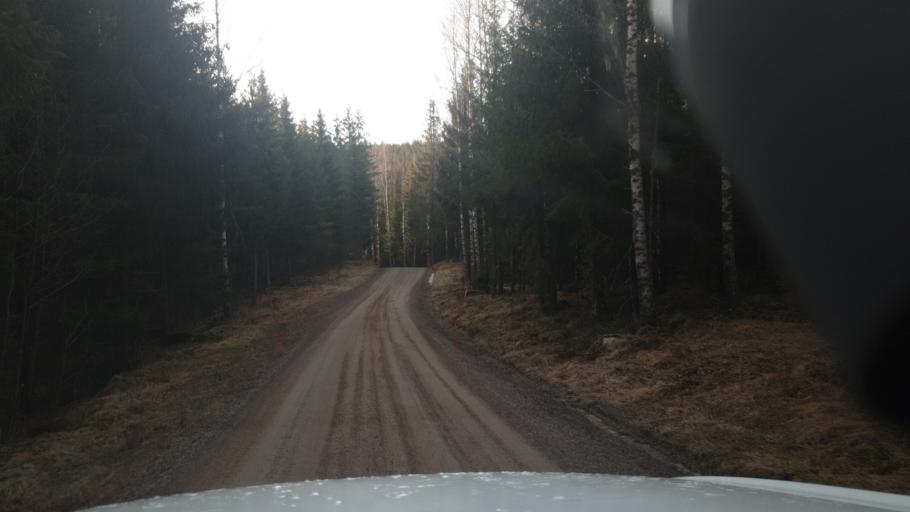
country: SE
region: Vaermland
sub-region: Eda Kommun
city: Amotfors
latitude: 59.8239
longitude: 12.4079
